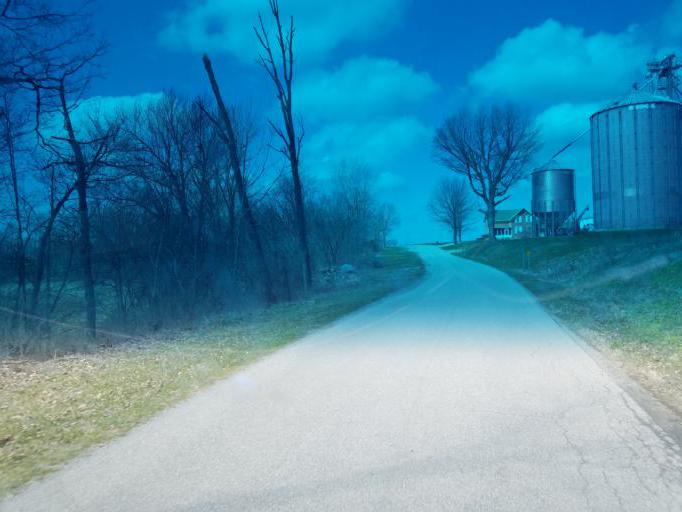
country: US
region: Ohio
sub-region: Crawford County
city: Bucyrus
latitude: 40.7990
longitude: -83.0178
